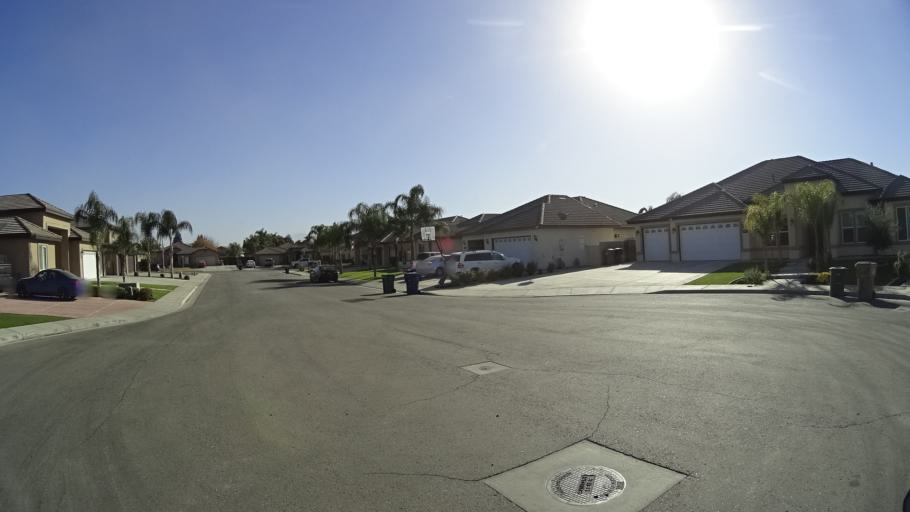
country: US
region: California
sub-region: Kern County
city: Greenfield
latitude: 35.2737
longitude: -119.0472
